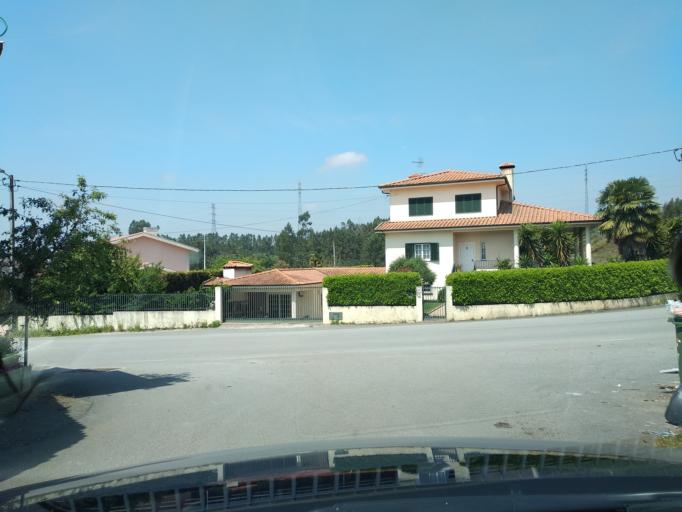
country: PT
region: Porto
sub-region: Valongo
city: Sobrado
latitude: 41.2078
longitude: -8.4438
